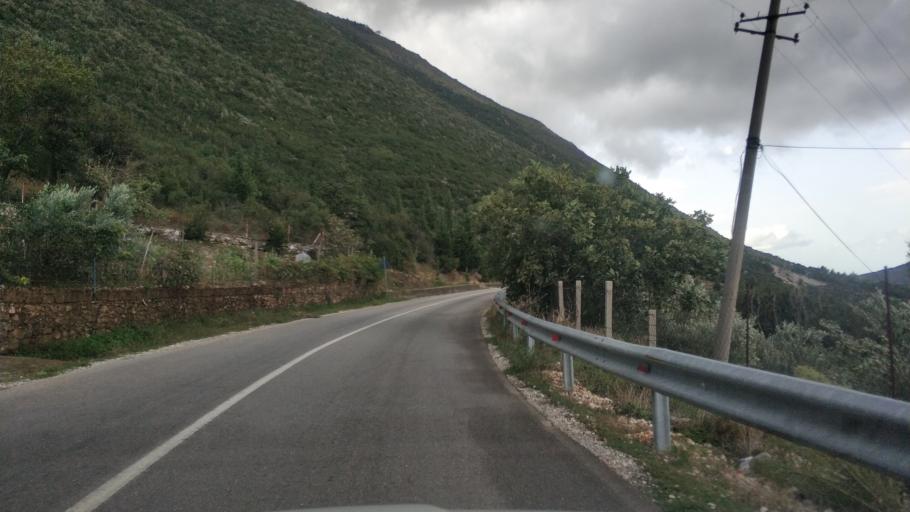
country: AL
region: Vlore
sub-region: Rrethi i Vlores
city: Brataj
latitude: 40.2368
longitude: 19.5543
